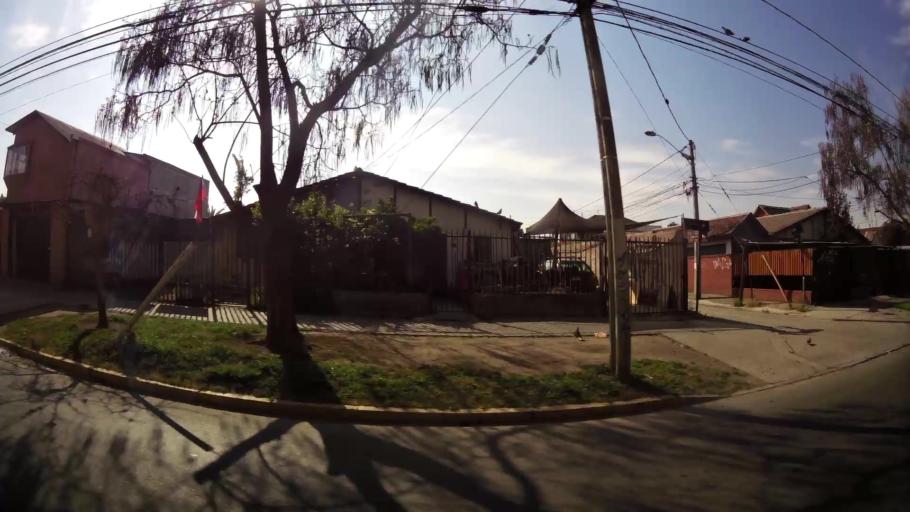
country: CL
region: Santiago Metropolitan
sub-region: Provincia de Santiago
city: Lo Prado
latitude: -33.4652
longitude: -70.7375
